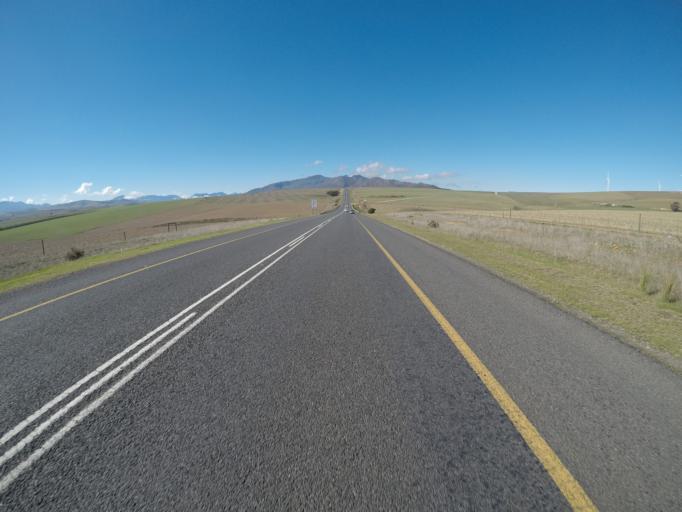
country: ZA
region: Western Cape
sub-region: Overberg District Municipality
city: Caledon
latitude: -34.2113
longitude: 19.3683
